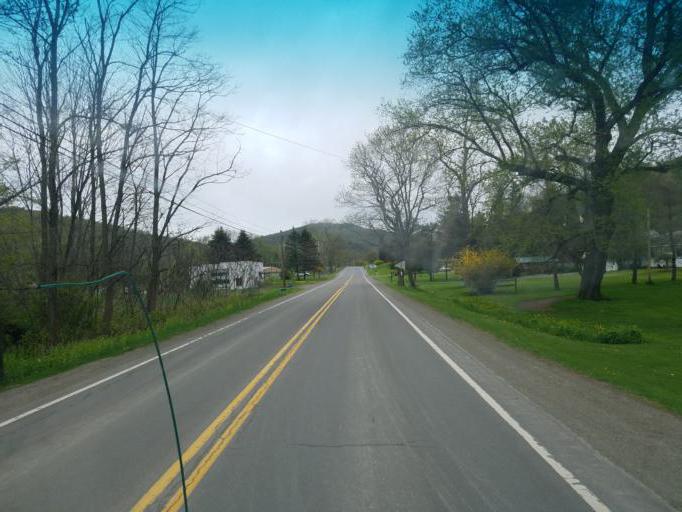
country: US
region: Pennsylvania
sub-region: Tioga County
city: Westfield
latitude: 41.9138
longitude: -77.6059
